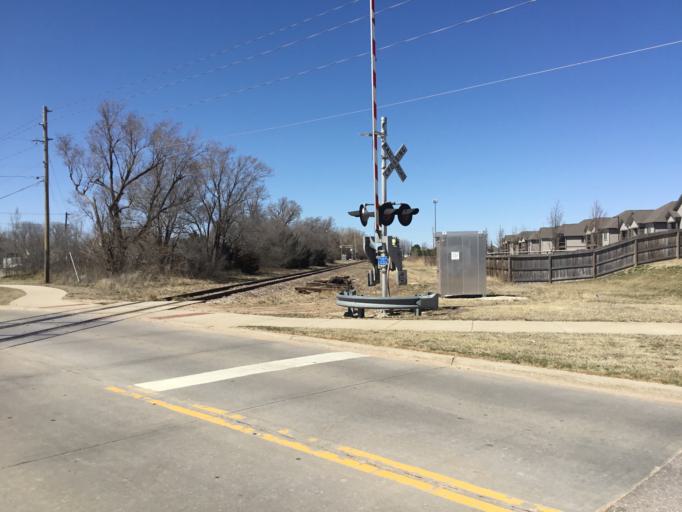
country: US
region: Kansas
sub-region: Sedgwick County
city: Maize
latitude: 37.7377
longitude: -97.4241
